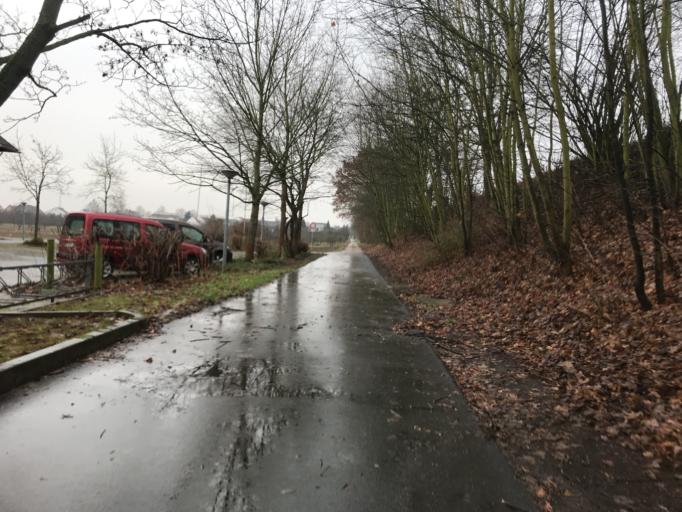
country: DE
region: Rheinland-Pfalz
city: Wackernheim
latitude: 49.9960
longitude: 8.1031
